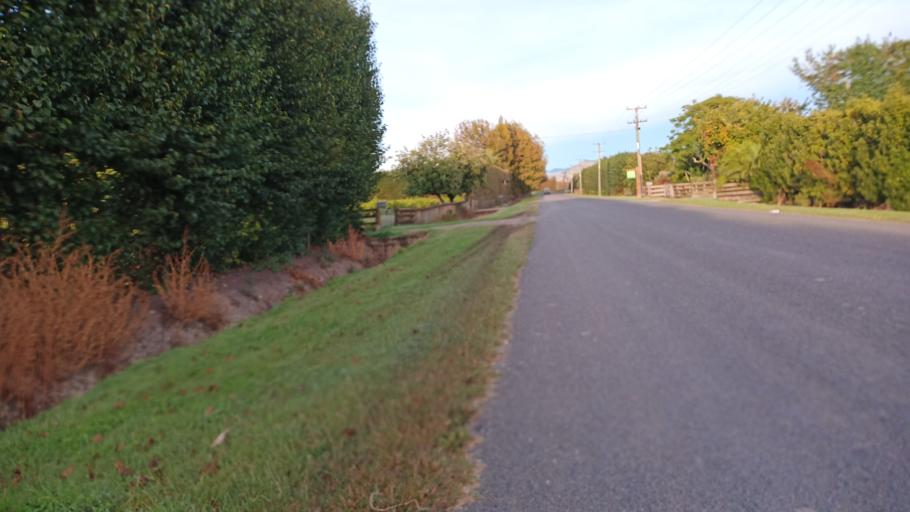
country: NZ
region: Gisborne
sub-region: Gisborne District
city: Gisborne
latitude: -38.6534
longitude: 177.9383
